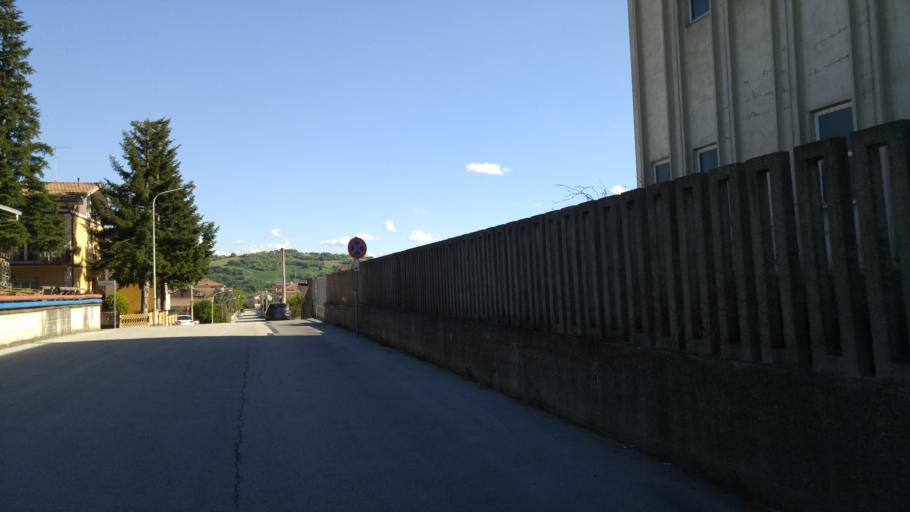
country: IT
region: The Marches
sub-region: Provincia di Pesaro e Urbino
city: Tavernelle
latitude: 43.7373
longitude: 12.8959
